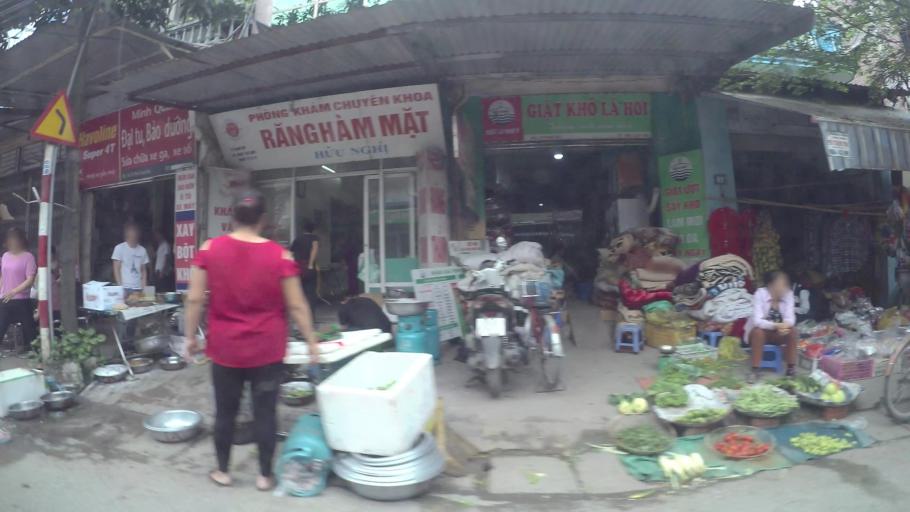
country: VN
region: Ha Noi
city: Hai BaTrung
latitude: 20.9854
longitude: 105.8883
